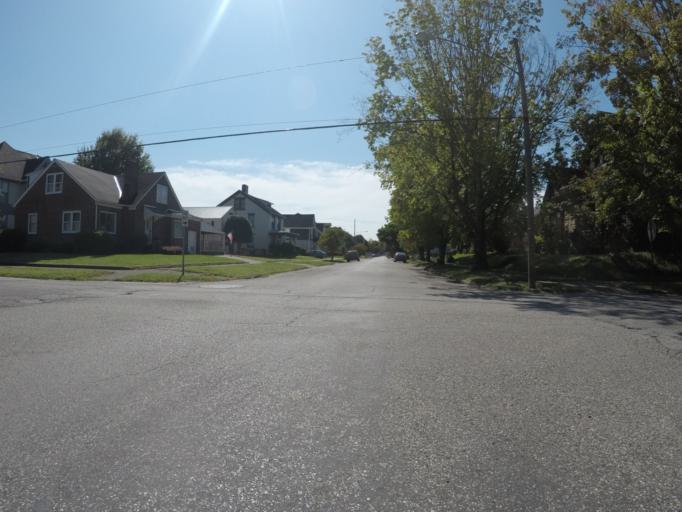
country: US
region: Ohio
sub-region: Lawrence County
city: Ironton
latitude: 38.5335
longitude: -82.6810
